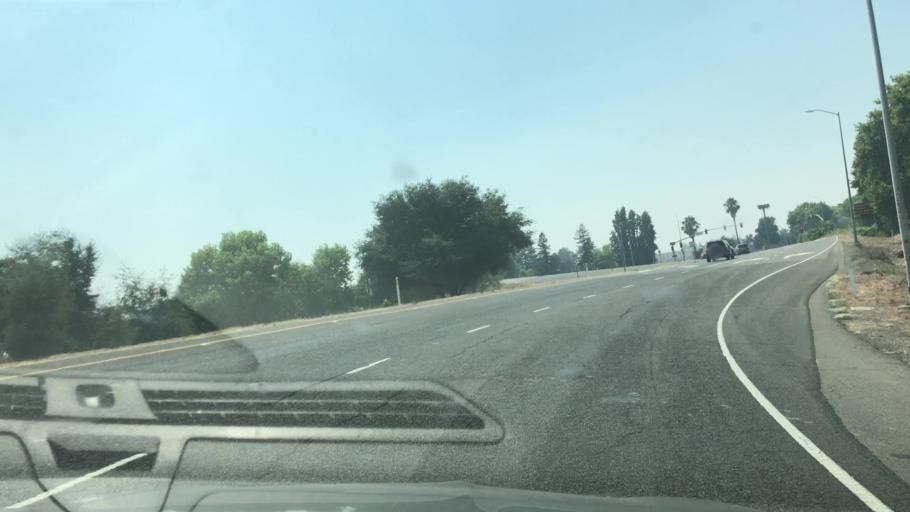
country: US
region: California
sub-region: Sacramento County
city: La Riviera
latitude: 38.5677
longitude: -121.3339
